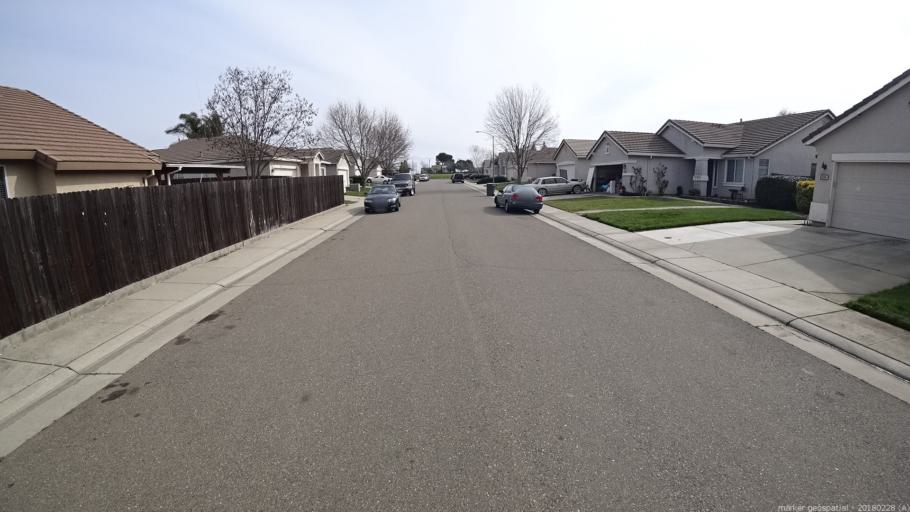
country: US
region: California
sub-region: Sacramento County
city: Antelope
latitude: 38.7186
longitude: -121.3306
